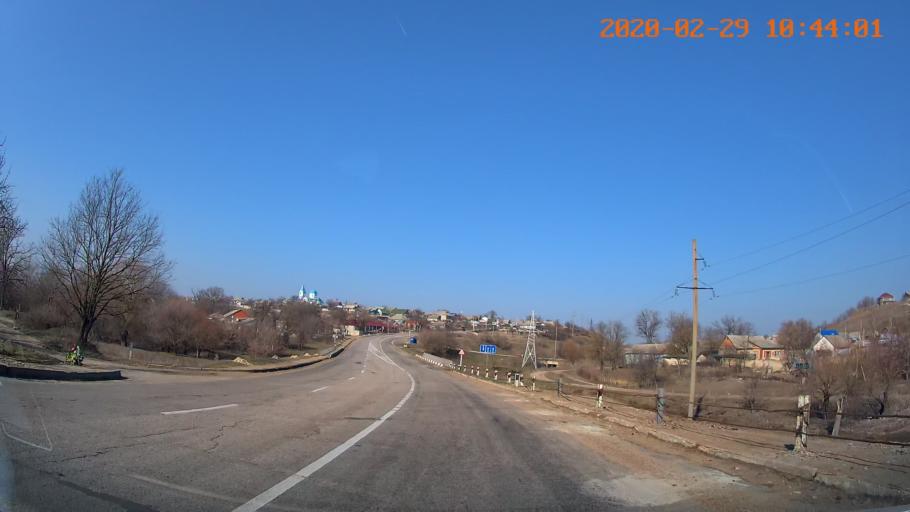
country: MD
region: Telenesti
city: Grigoriopol
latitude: 47.0674
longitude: 29.4000
